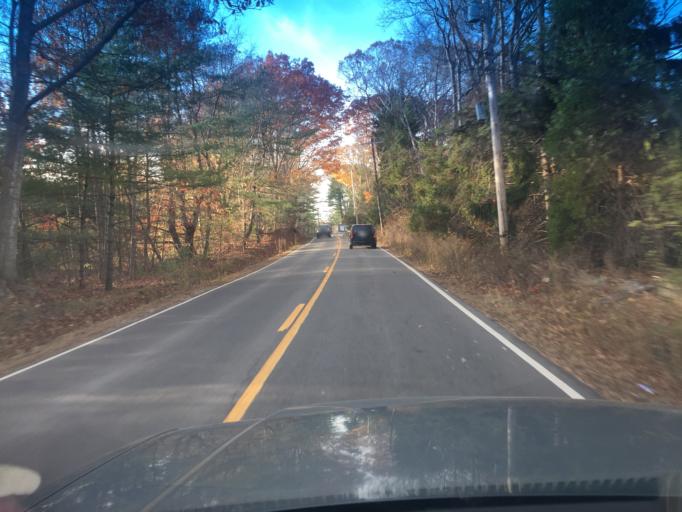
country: US
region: Maine
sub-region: York County
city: Eliot
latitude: 43.1851
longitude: -70.7423
